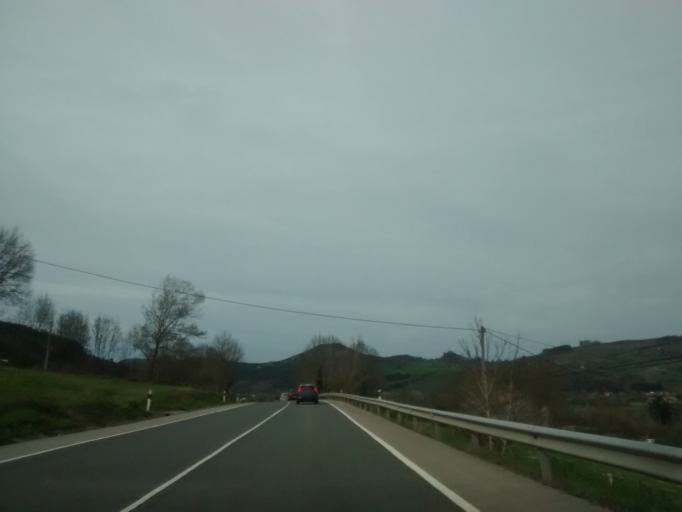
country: ES
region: Cantabria
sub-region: Provincia de Cantabria
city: Corvera
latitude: 43.2597
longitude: -3.9477
